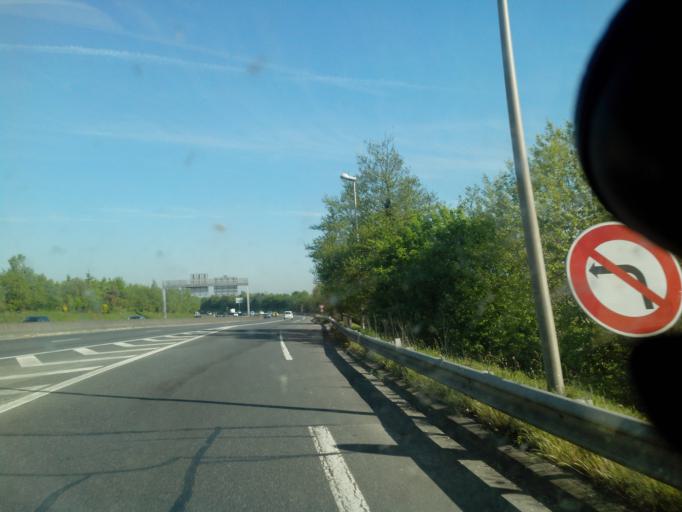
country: FR
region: Pays de la Loire
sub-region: Departement de la Loire-Atlantique
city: Saint-Herblain
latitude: 47.2270
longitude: -1.6216
